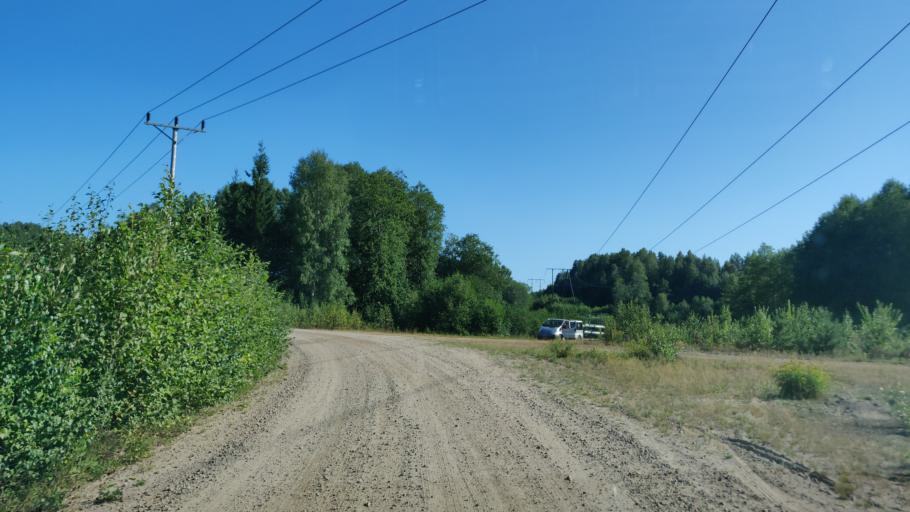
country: SE
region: Vaermland
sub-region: Hagfors Kommun
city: Ekshaerad
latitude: 60.0492
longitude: 13.5230
